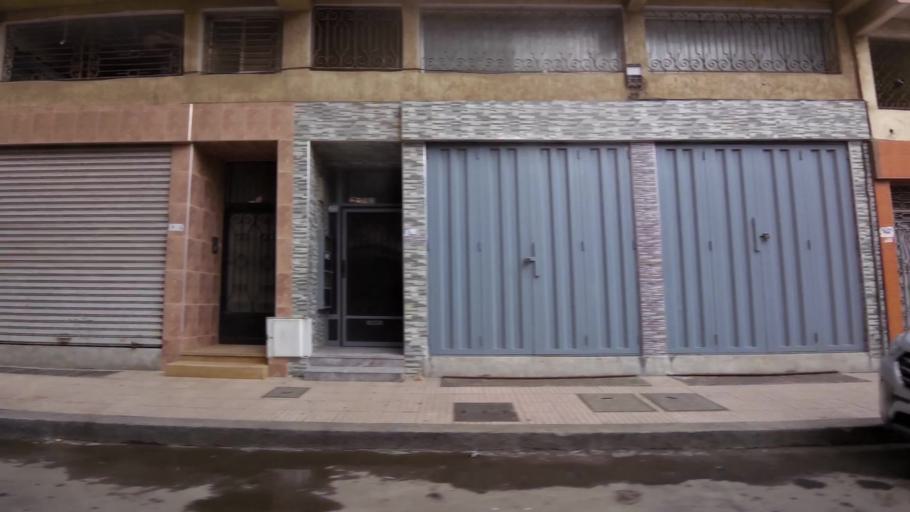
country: MA
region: Grand Casablanca
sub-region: Casablanca
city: Casablanca
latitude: 33.5429
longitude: -7.6817
